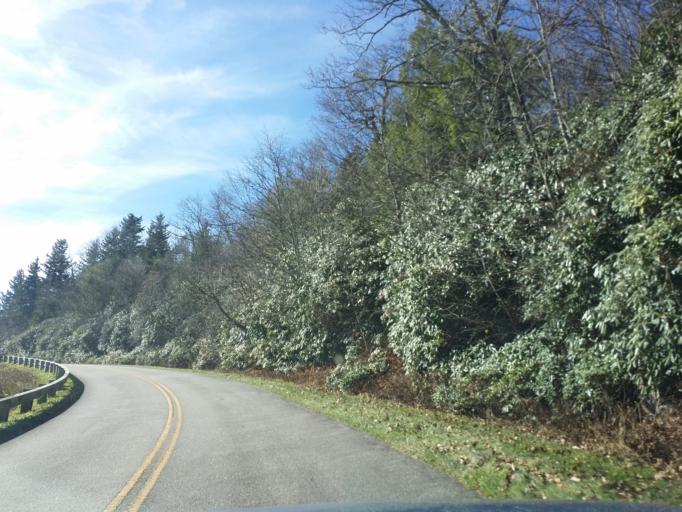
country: US
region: North Carolina
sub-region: Buncombe County
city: Black Mountain
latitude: 35.7240
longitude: -82.2156
